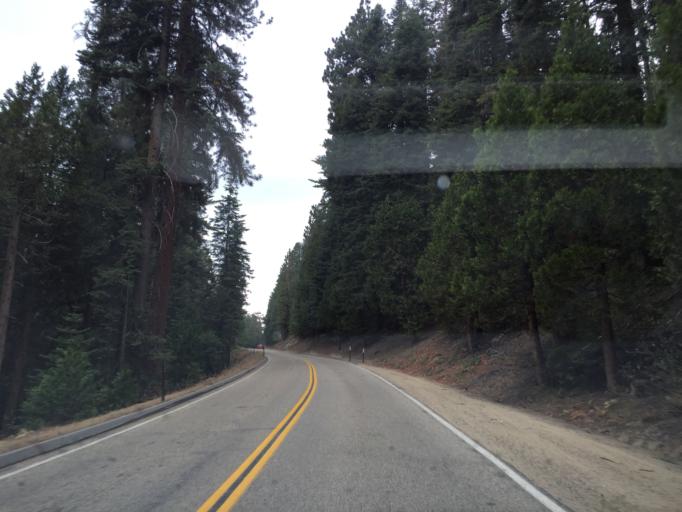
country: US
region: California
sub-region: Tulare County
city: Three Rivers
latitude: 36.7192
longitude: -118.9478
